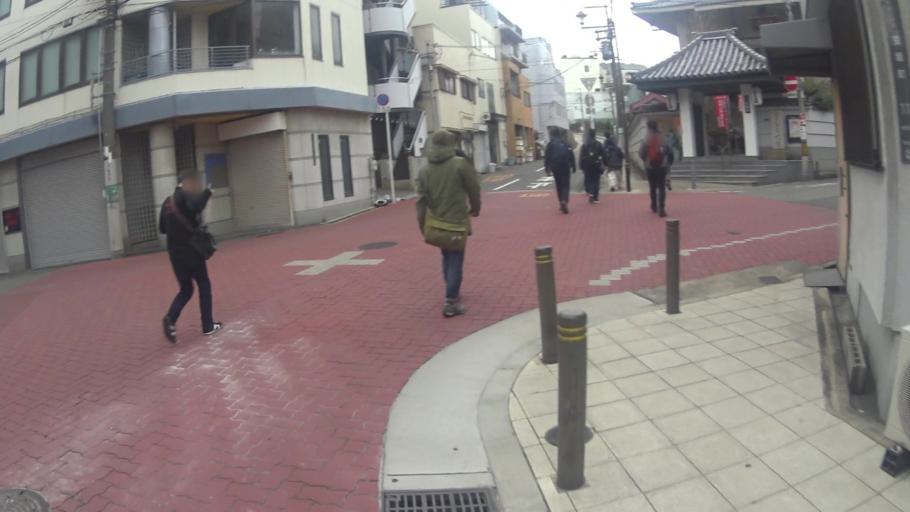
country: JP
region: Osaka
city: Osaka-shi
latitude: 34.6741
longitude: 135.5271
